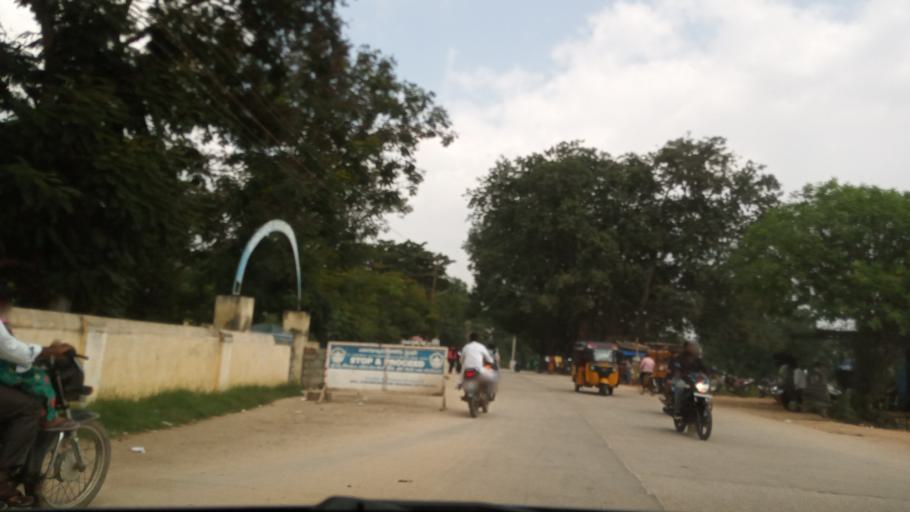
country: IN
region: Andhra Pradesh
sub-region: Chittoor
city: Madanapalle
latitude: 13.6391
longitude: 78.6328
